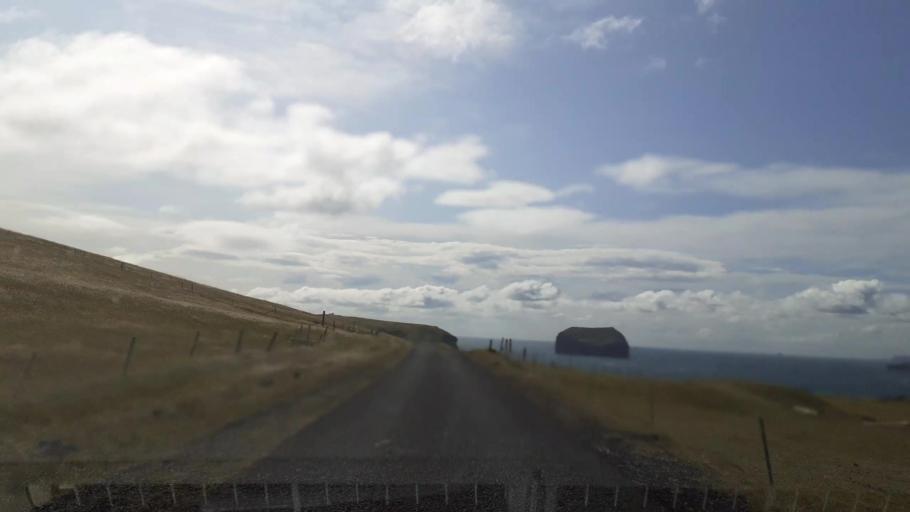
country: IS
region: South
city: Vestmannaeyjar
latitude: 63.4196
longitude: -20.2805
